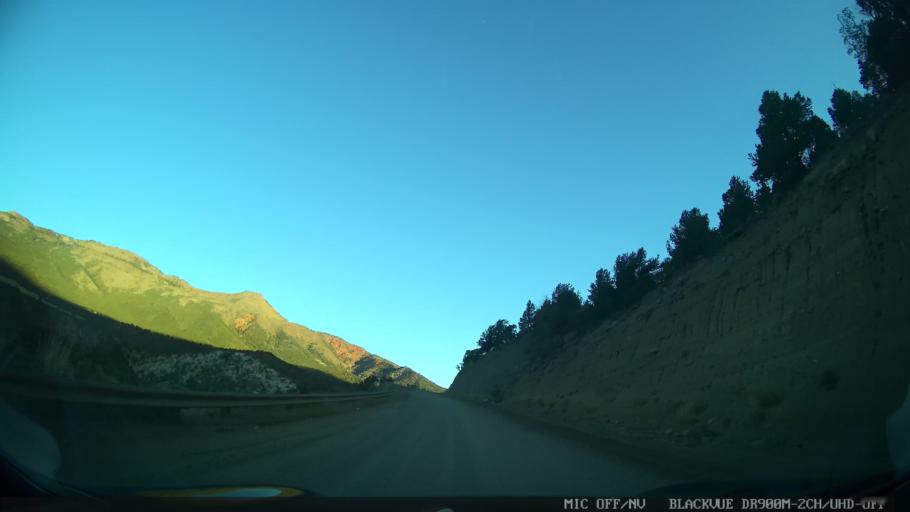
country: US
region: Colorado
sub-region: Eagle County
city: Edwards
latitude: 39.8967
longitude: -106.6069
